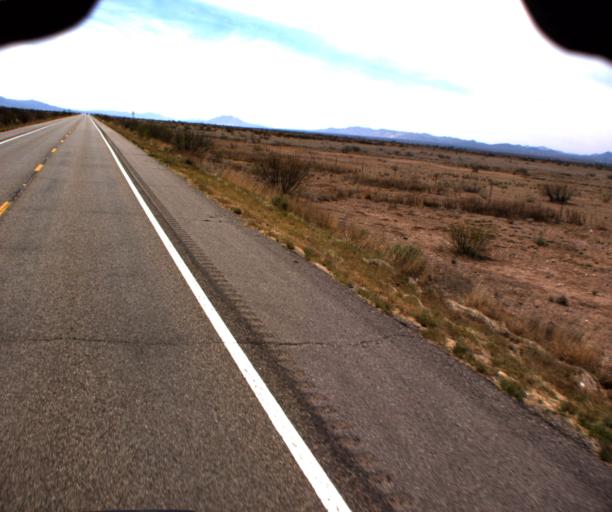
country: US
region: Arizona
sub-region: Cochise County
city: Pirtleville
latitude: 31.4946
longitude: -109.6320
